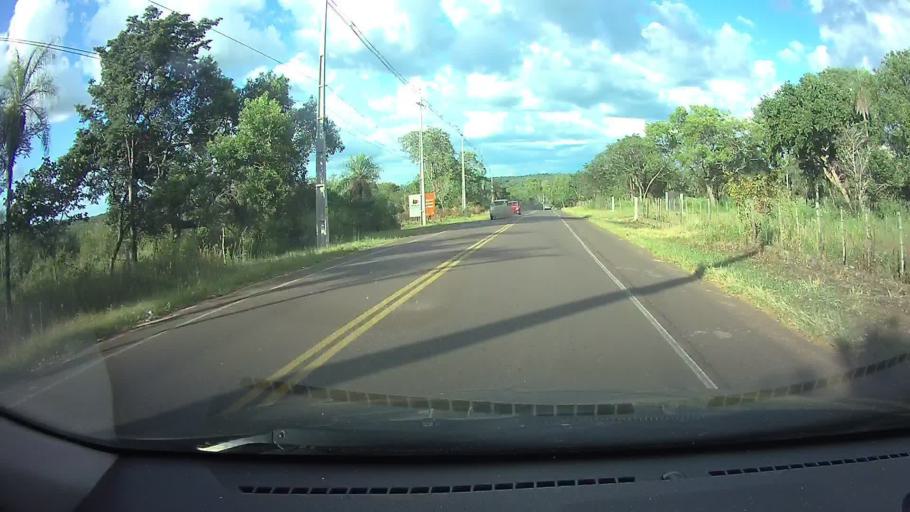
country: PY
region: Cordillera
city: Altos
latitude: -25.2492
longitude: -57.2370
